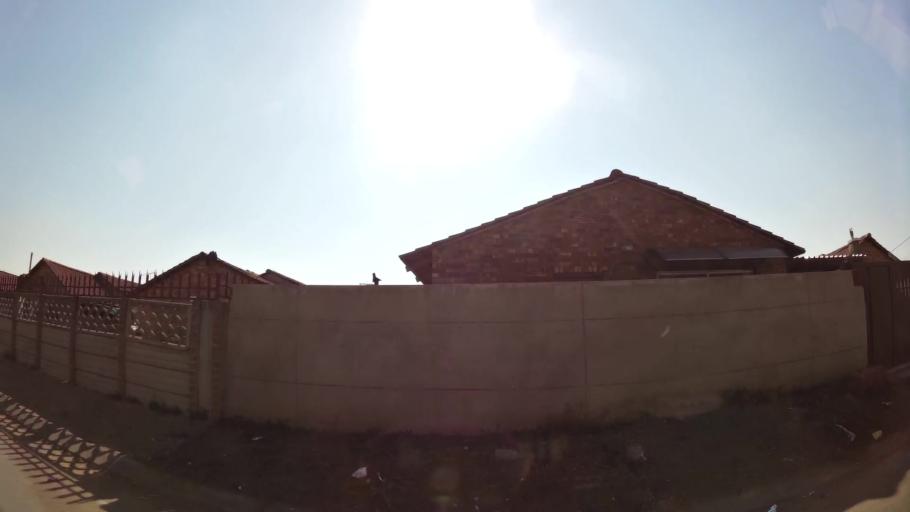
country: ZA
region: Gauteng
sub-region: Ekurhuleni Metropolitan Municipality
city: Boksburg
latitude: -26.2238
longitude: 28.2961
